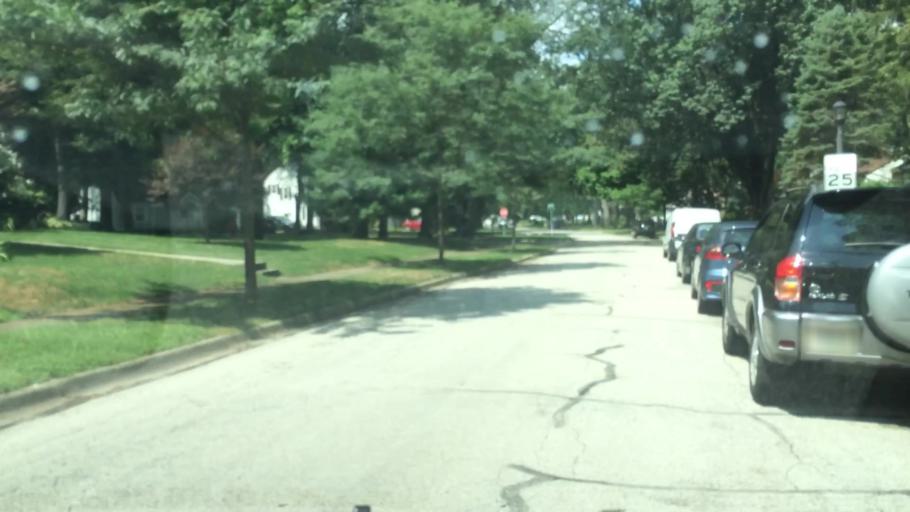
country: US
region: Ohio
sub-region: Summit County
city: Silver Lake
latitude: 41.1454
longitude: -81.4629
